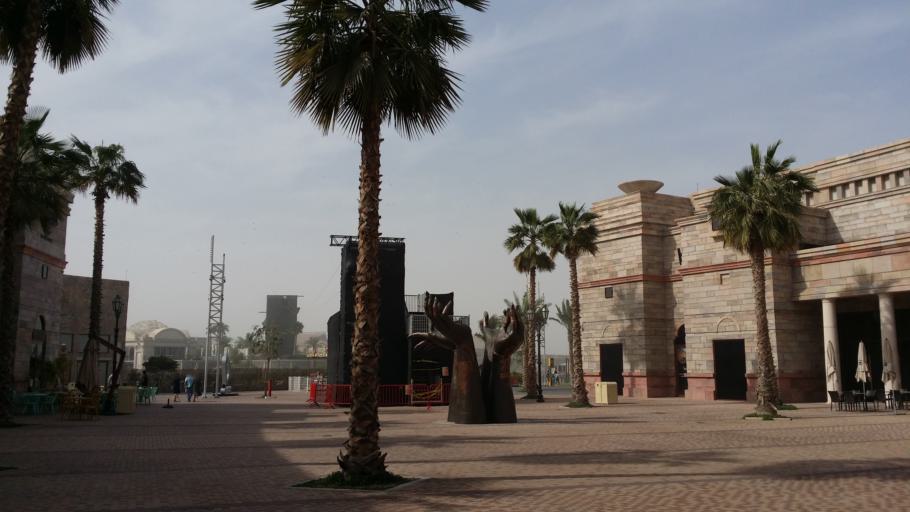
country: AE
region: Dubai
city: Dubai
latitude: 24.9204
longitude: 55.0092
